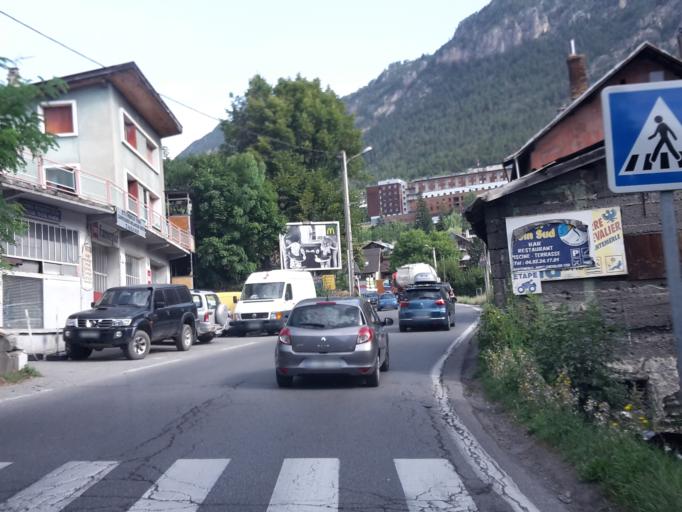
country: FR
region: Provence-Alpes-Cote d'Azur
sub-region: Departement des Hautes-Alpes
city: Briancon
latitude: 44.9014
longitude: 6.6313
